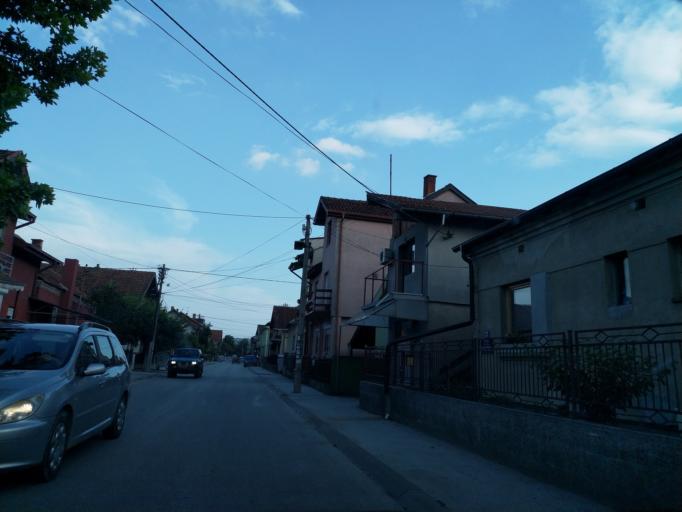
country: RS
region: Central Serbia
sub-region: Pomoravski Okrug
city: Jagodina
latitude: 43.9826
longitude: 21.2434
